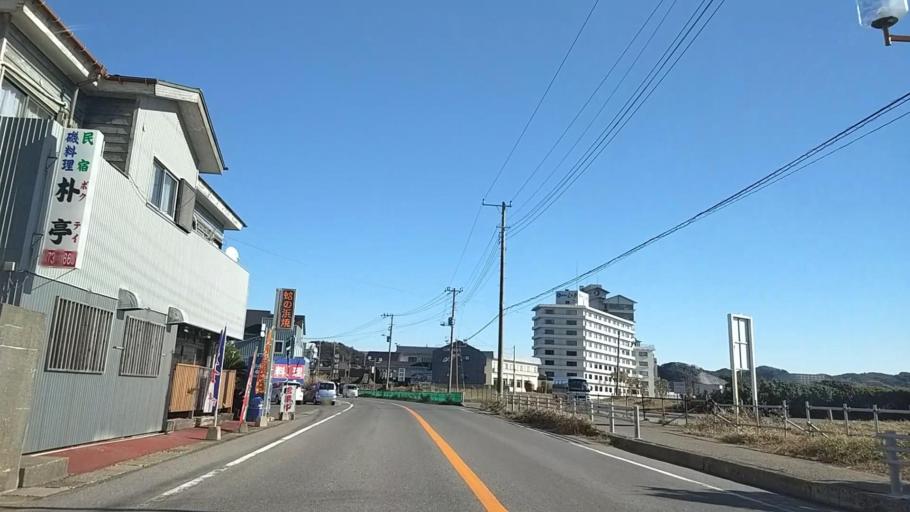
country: JP
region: Chiba
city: Katsuura
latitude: 35.1510
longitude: 140.3065
